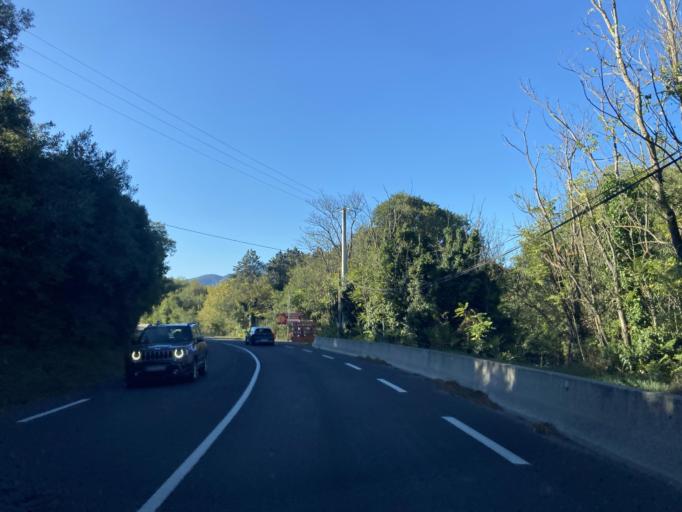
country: FR
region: Languedoc-Roussillon
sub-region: Departement des Pyrenees-Orientales
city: el Volo
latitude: 42.5071
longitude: 2.8240
